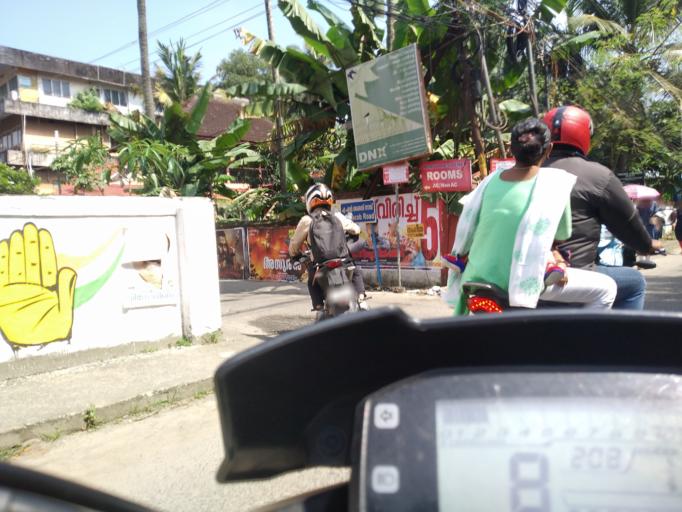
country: IN
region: Kerala
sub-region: Ernakulam
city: Cochin
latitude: 9.9795
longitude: 76.2845
